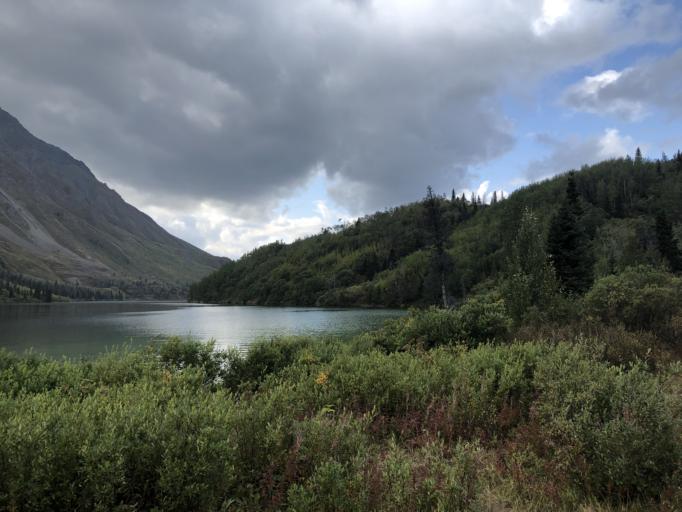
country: CA
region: Yukon
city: Haines Junction
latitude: 60.3192
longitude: -137.1033
